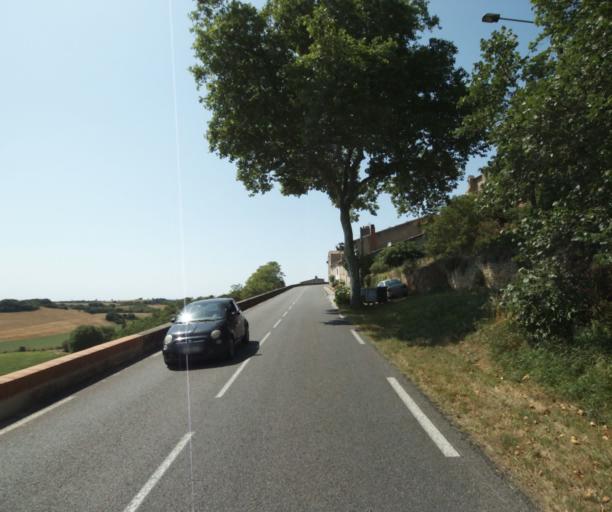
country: FR
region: Midi-Pyrenees
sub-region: Departement de la Haute-Garonne
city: Saint-Felix-Lauragais
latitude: 43.4483
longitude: 1.8870
